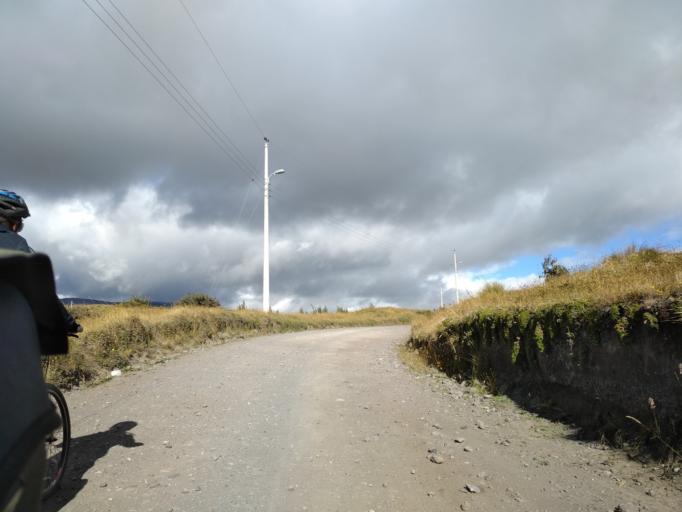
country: EC
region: Pichincha
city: Machachi
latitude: -0.5561
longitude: -78.4548
